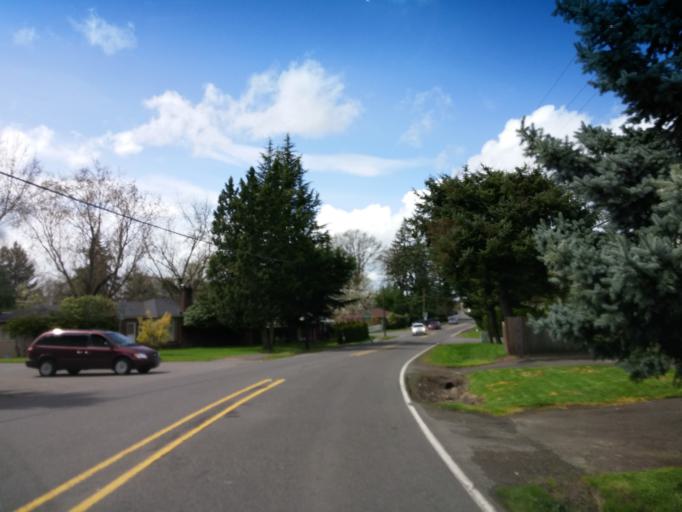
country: US
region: Oregon
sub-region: Washington County
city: Cedar Hills
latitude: 45.4999
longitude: -122.8010
